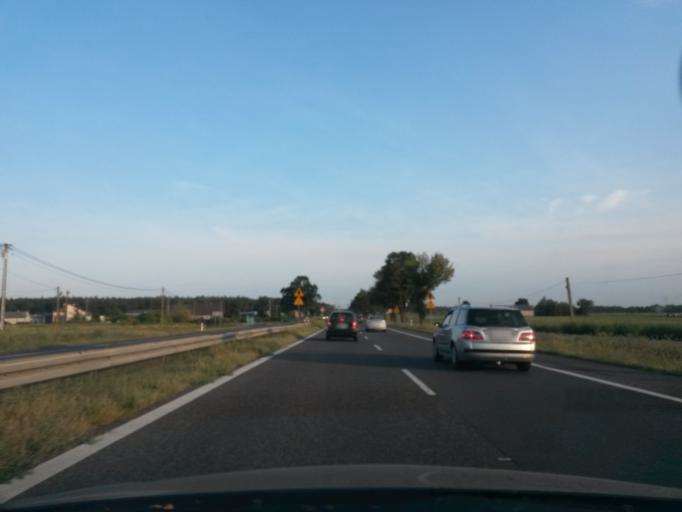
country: PL
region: Masovian Voivodeship
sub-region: Powiat nowodworski
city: Zakroczym
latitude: 52.4644
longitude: 20.5733
